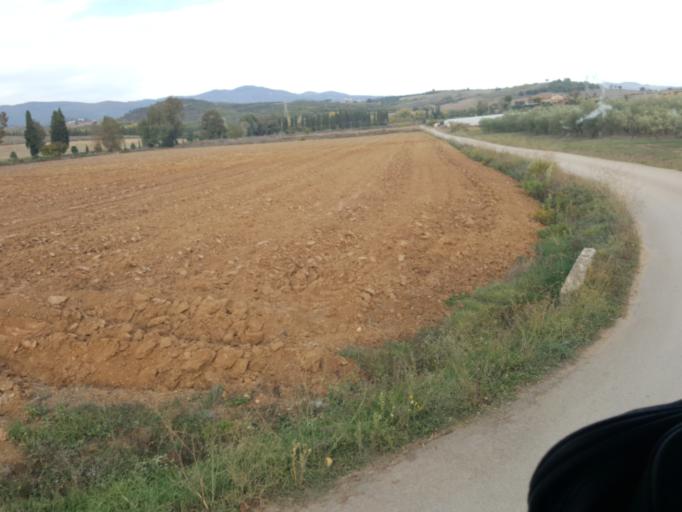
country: IT
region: Tuscany
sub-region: Provincia di Grosseto
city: Ribolla
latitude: 42.9505
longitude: 10.9954
